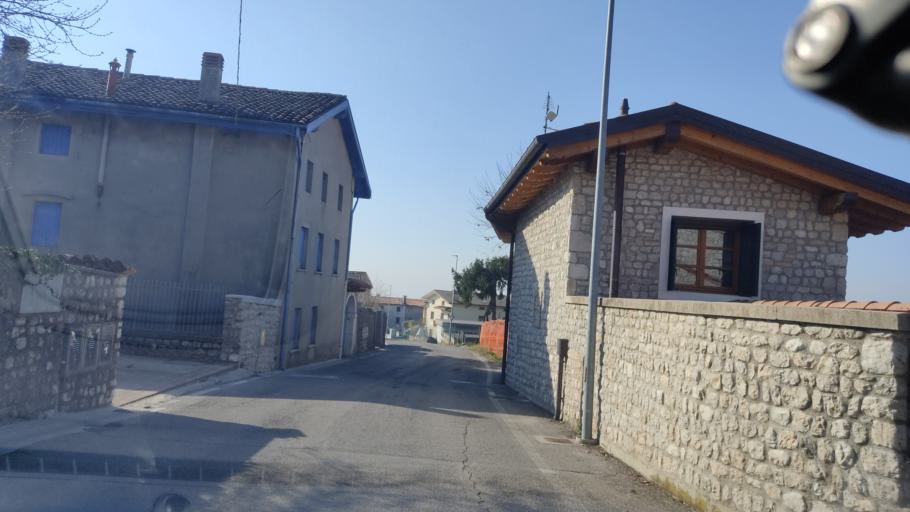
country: IT
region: Friuli Venezia Giulia
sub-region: Provincia di Pordenone
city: Budoia
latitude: 46.0527
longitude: 12.5331
